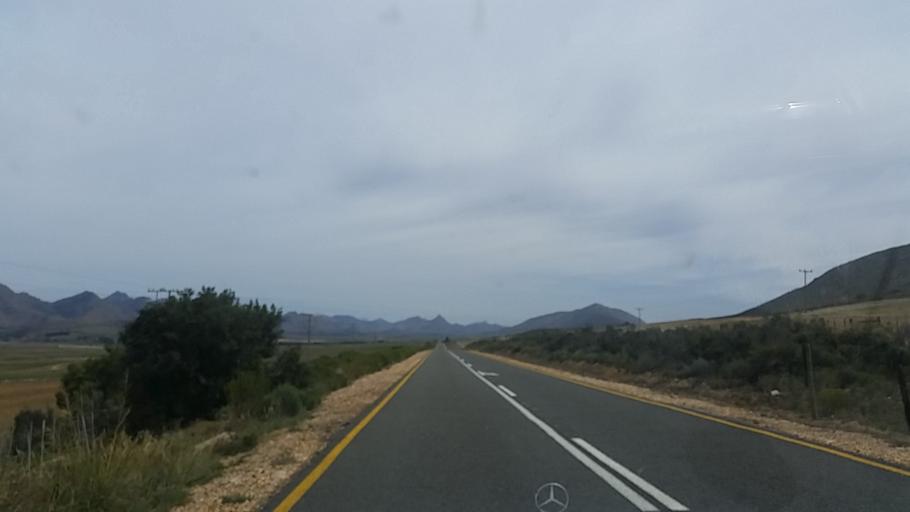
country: ZA
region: Western Cape
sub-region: Eden District Municipality
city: George
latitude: -33.7942
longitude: 22.6189
